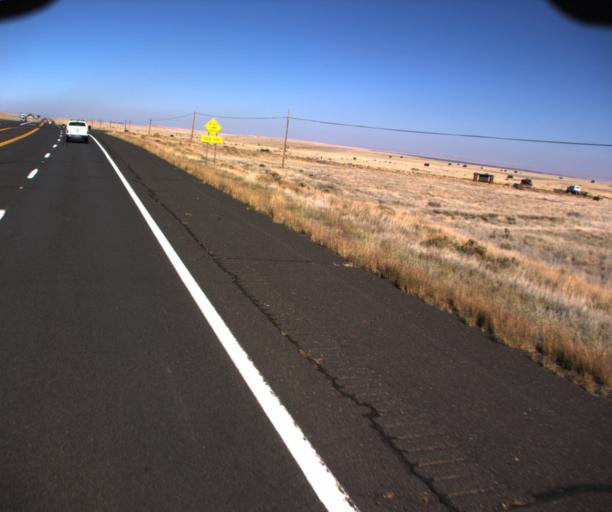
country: US
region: Arizona
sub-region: Coconino County
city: Flagstaff
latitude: 35.5737
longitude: -111.5310
